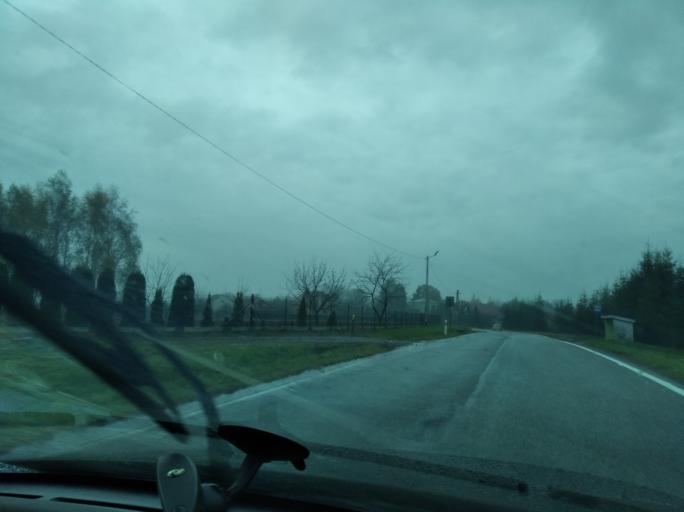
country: PL
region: Subcarpathian Voivodeship
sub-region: Powiat lancucki
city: Handzlowka
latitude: 50.0050
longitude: 22.2123
